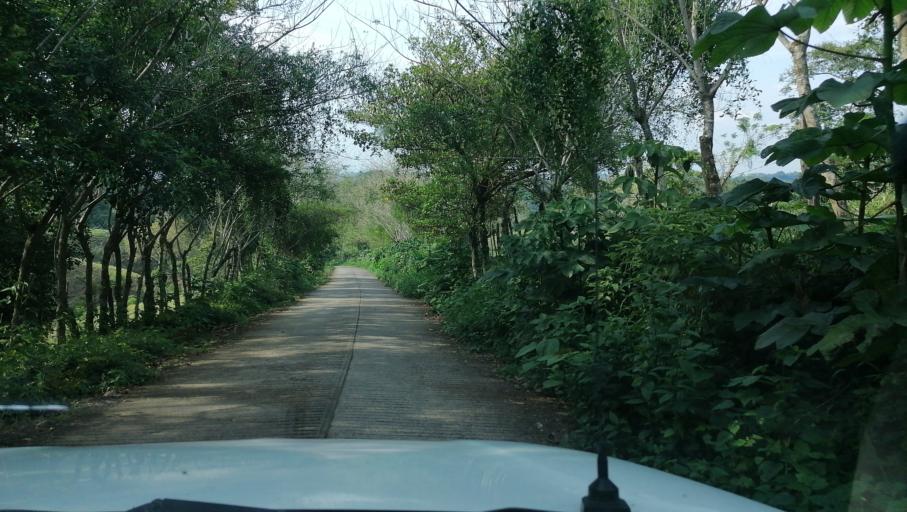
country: MX
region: Chiapas
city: Ostuacan
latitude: 17.4821
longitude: -93.2398
